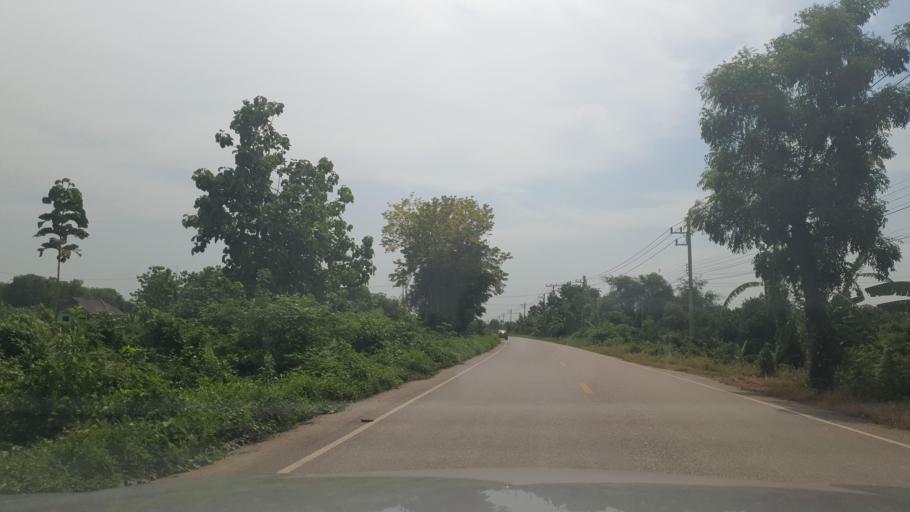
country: TH
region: Sukhothai
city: Si Samrong
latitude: 17.1154
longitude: 99.8867
